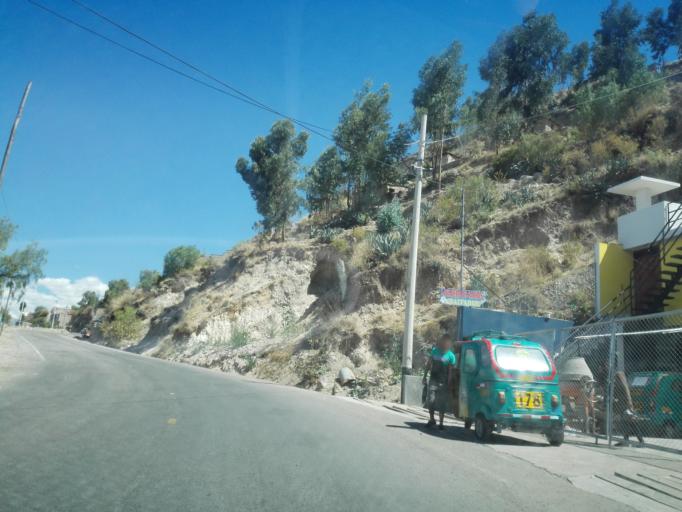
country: PE
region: Ayacucho
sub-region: Provincia de Huamanga
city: Ayacucho
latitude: -13.1631
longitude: -74.2400
